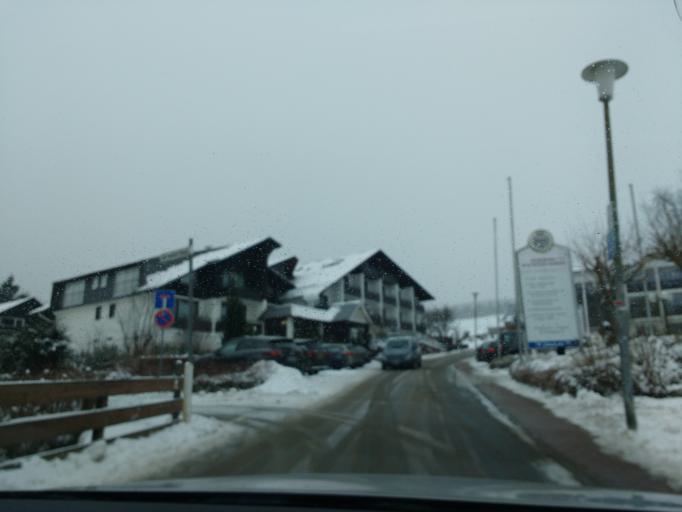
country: DE
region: Hesse
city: Willingen
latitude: 51.2950
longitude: 8.6017
